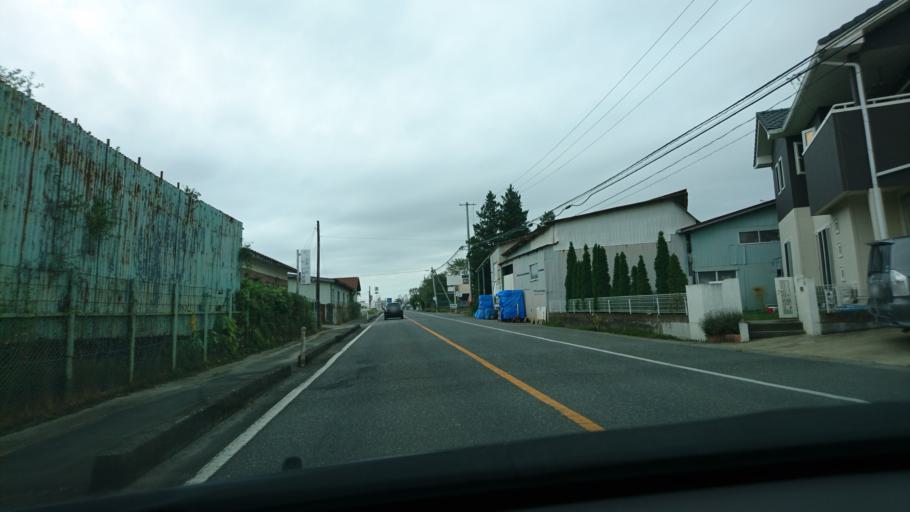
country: JP
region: Iwate
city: Ichinoseki
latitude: 38.7584
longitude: 141.0747
